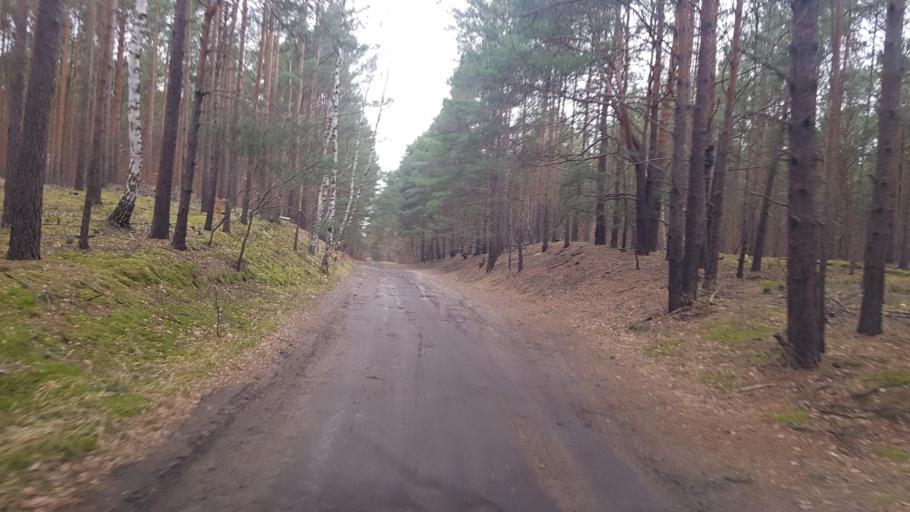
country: DE
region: Brandenburg
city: Halbe
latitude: 52.0638
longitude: 13.6757
